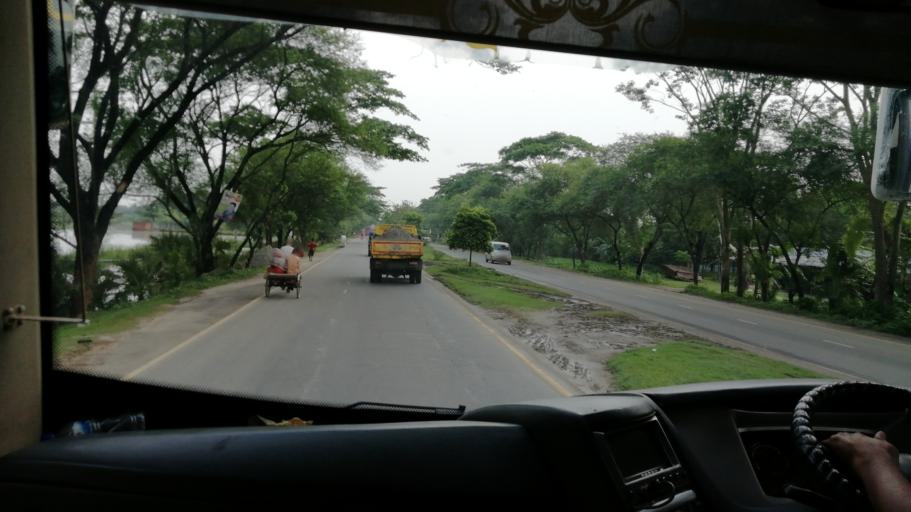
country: BD
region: Khulna
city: Khulna
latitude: 22.7903
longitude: 89.5328
